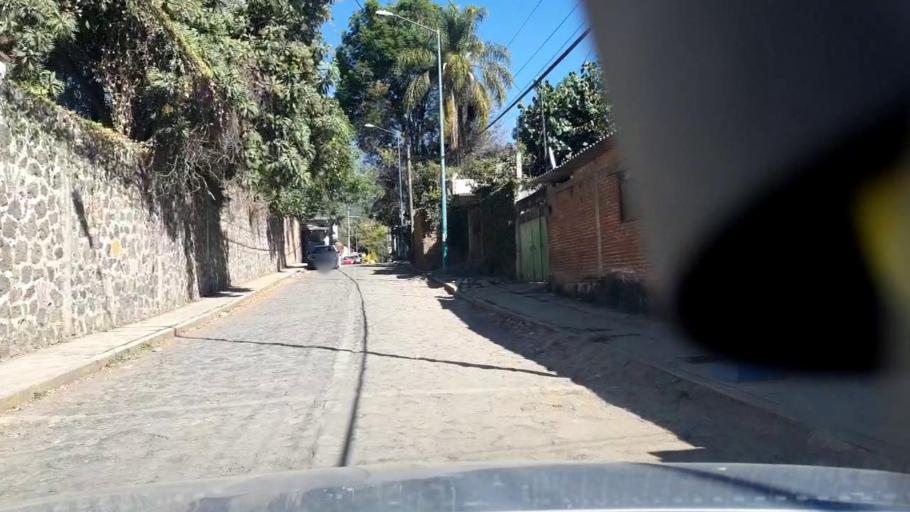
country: MX
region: Morelos
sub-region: Cuernavaca
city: Lomas de Ahuatepec
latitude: 18.9685
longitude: -99.2225
